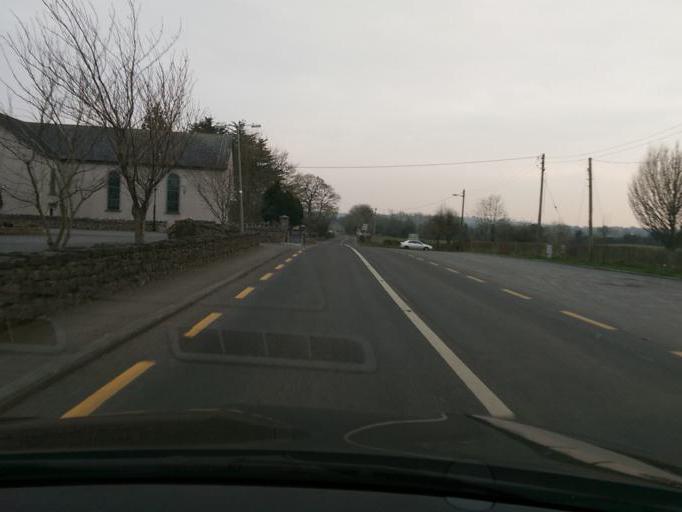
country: IE
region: Leinster
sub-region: An Longfort
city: Ballymahon
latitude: 53.5299
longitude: -7.7930
